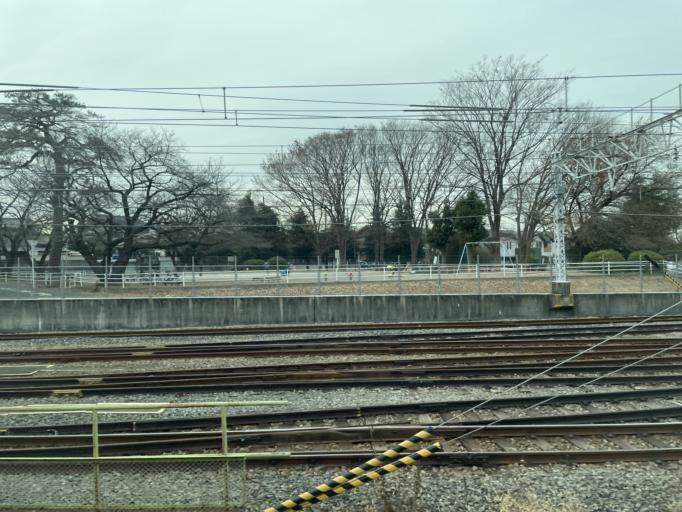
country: JP
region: Saitama
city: Hasuda
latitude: 35.9388
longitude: 139.6357
